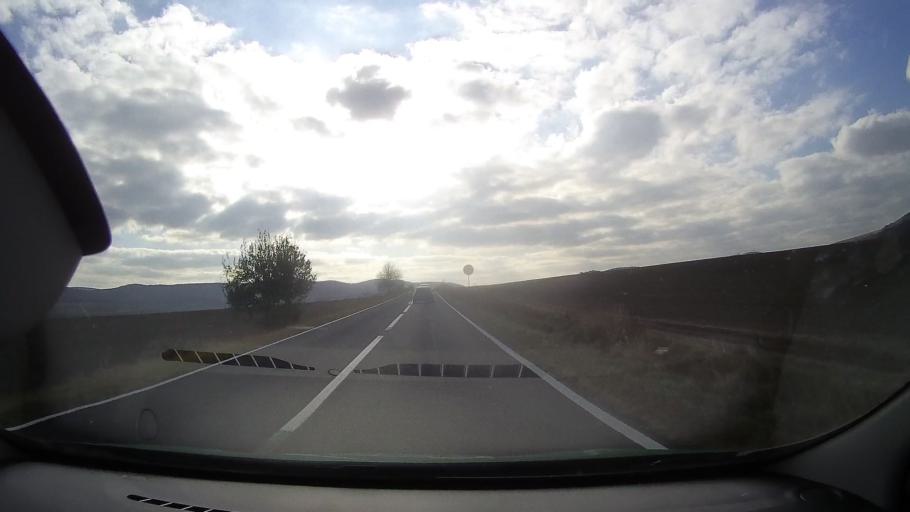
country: RO
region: Tulcea
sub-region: Comuna Nalbant
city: Nicolae Balcescu
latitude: 44.9819
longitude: 28.5506
